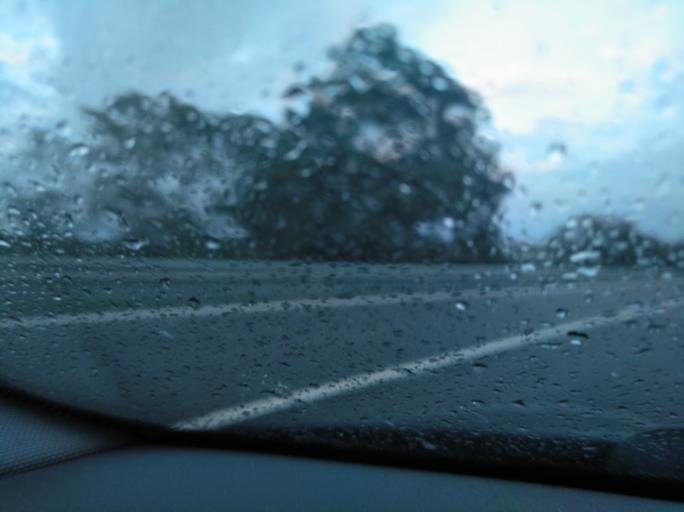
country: PT
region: Faro
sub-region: Castro Marim
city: Castro Marim
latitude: 37.2392
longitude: -7.4481
